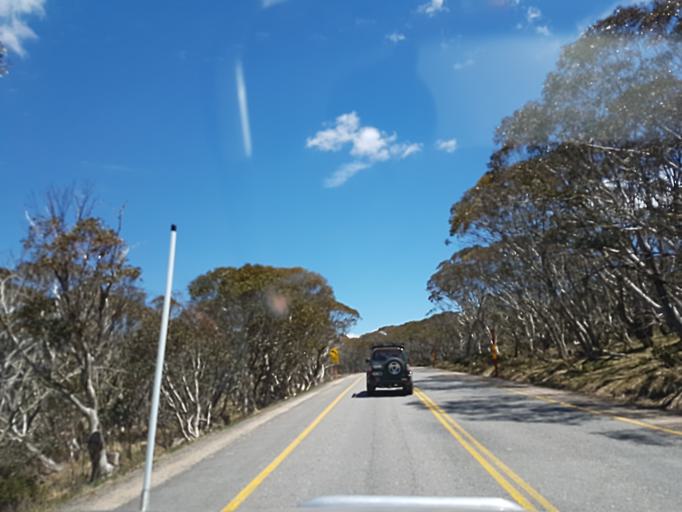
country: AU
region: Victoria
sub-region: Alpine
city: Mount Beauty
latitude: -37.0219
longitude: 147.2242
